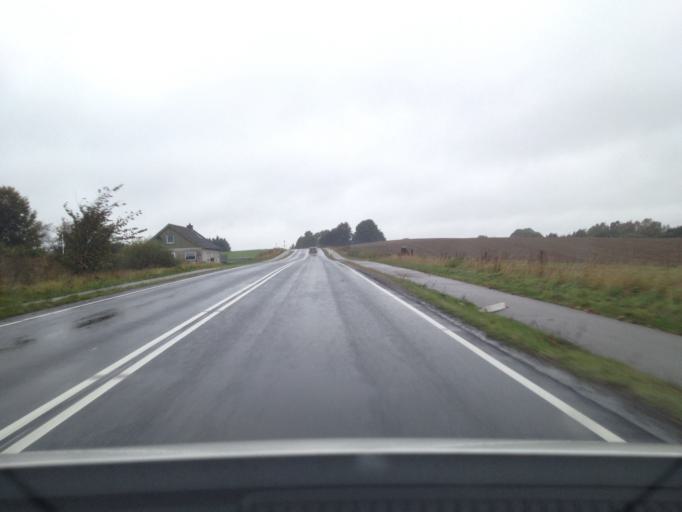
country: DK
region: Zealand
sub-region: Holbaek Kommune
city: Tollose
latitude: 55.5240
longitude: 11.7258
